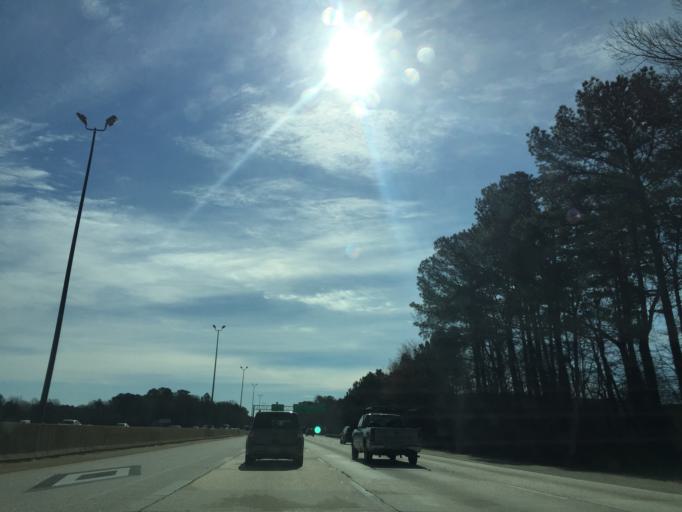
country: US
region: Virginia
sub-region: City of Newport News
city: Newport News
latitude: 37.0638
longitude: -76.4246
